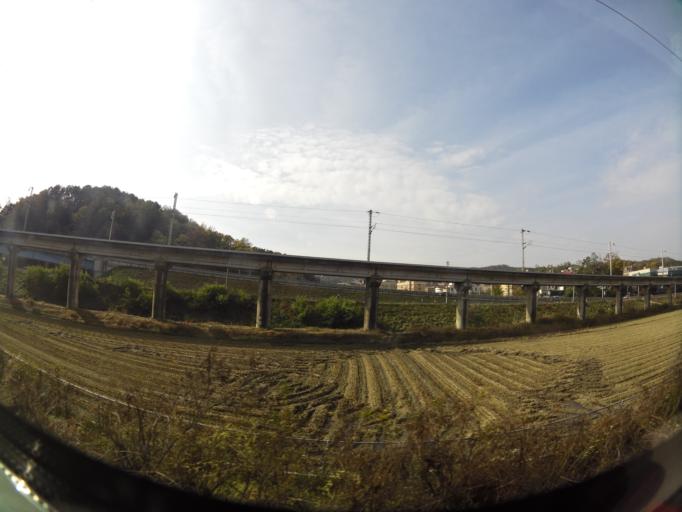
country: KR
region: Chungcheongbuk-do
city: Cheongju-si
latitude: 36.6180
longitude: 127.2926
